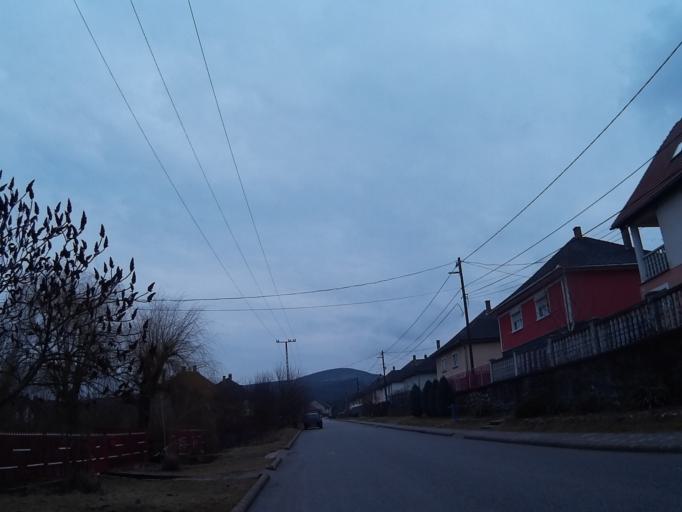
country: HU
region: Borsod-Abauj-Zemplen
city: Gonc
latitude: 48.5398
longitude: 21.4116
